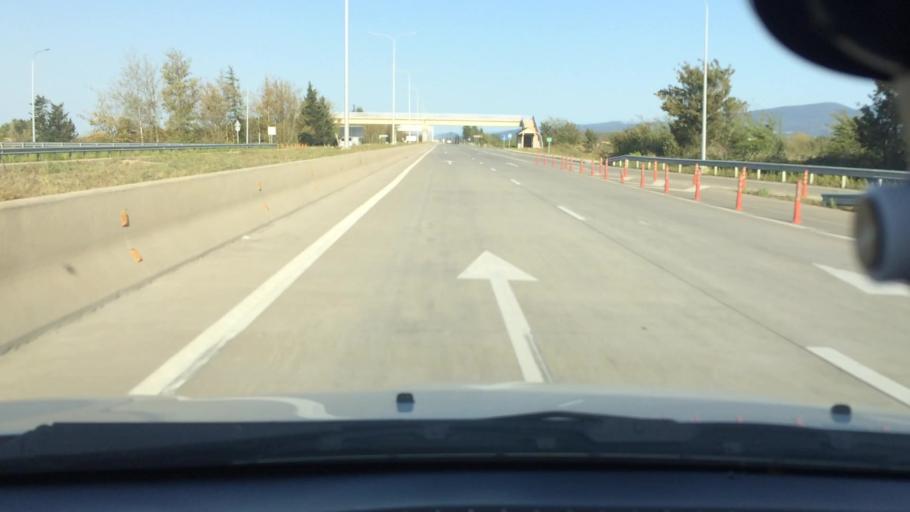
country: GE
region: Imereti
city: Zestap'oni
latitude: 42.1597
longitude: 42.9490
